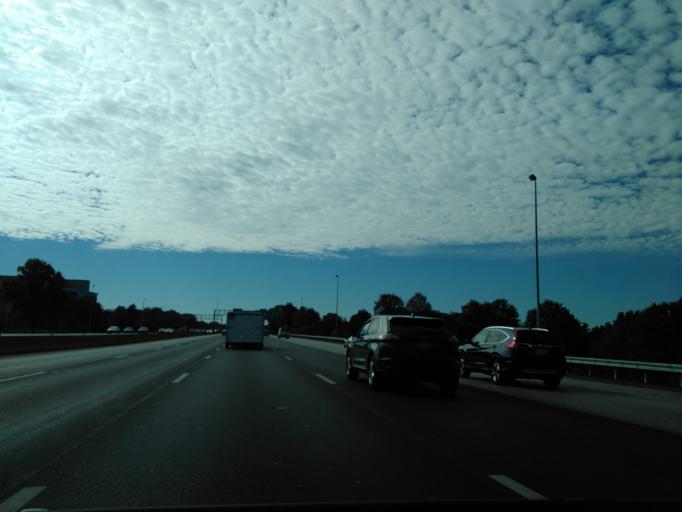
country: US
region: Missouri
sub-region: Saint Louis County
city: Creve Coeur
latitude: 38.6487
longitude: -90.4487
